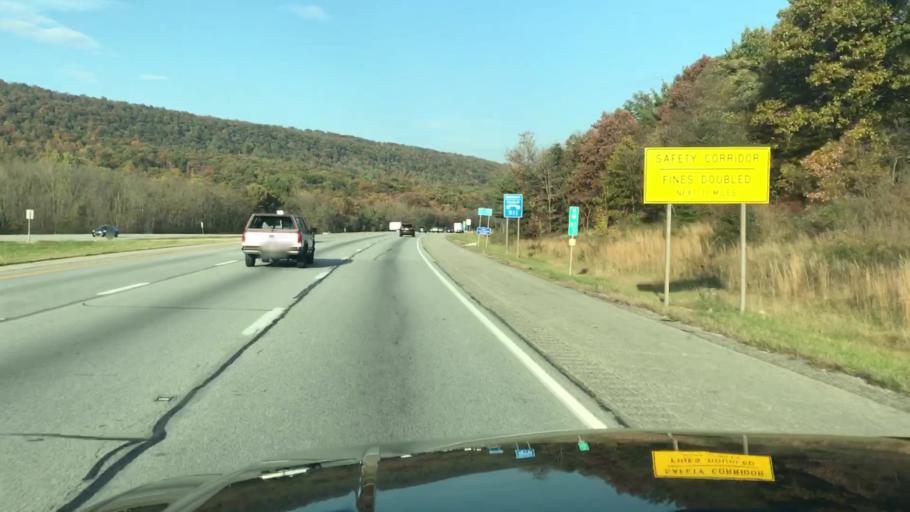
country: US
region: Pennsylvania
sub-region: Cumberland County
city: Enola
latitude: 40.2968
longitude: -76.9778
